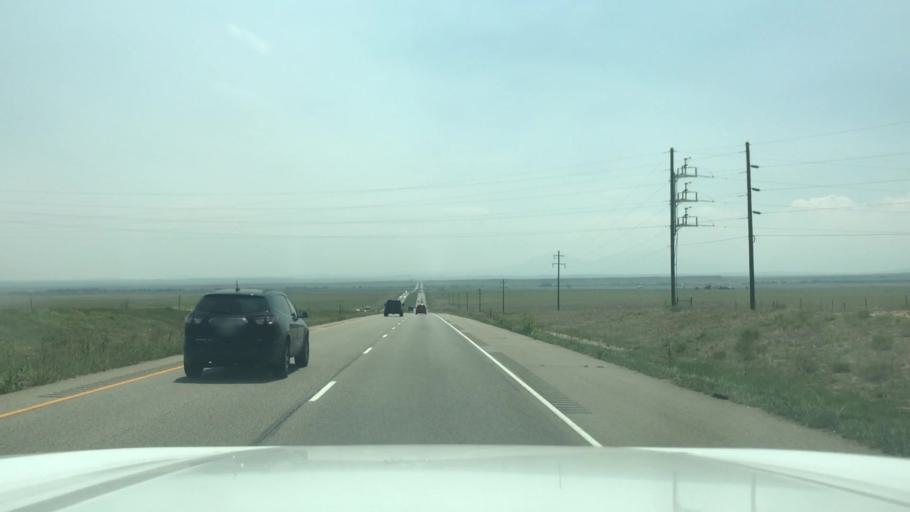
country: US
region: Colorado
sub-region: Pueblo County
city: Colorado City
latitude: 37.8877
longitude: -104.8292
